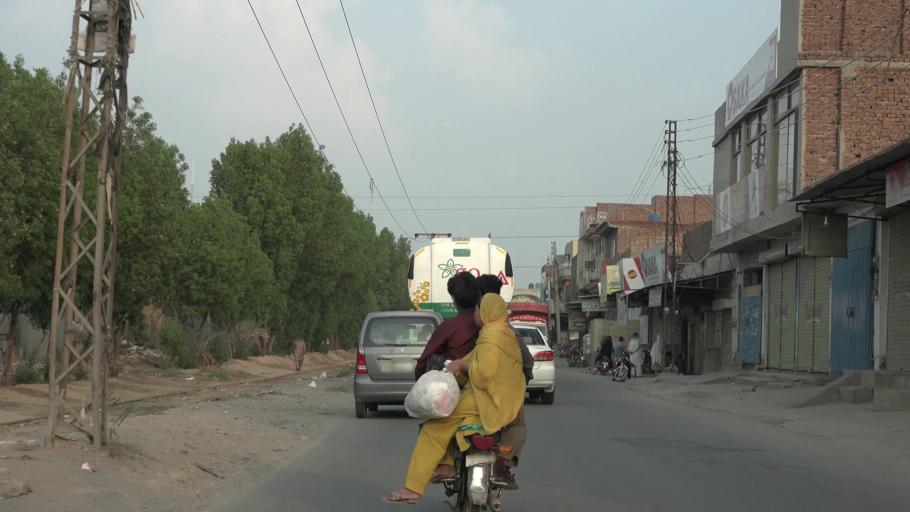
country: PK
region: Punjab
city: Faisalabad
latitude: 31.4514
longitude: 73.1220
